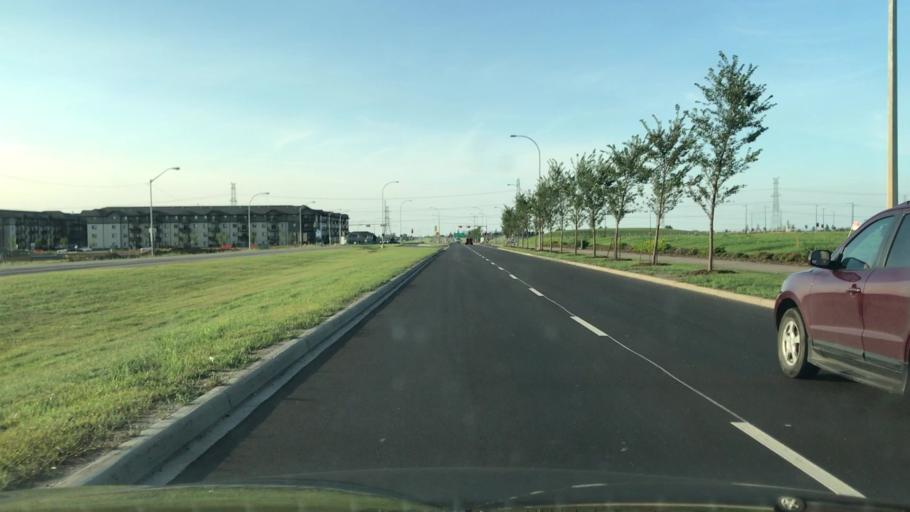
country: CA
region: Alberta
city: Beaumont
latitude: 53.4259
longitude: -113.4178
